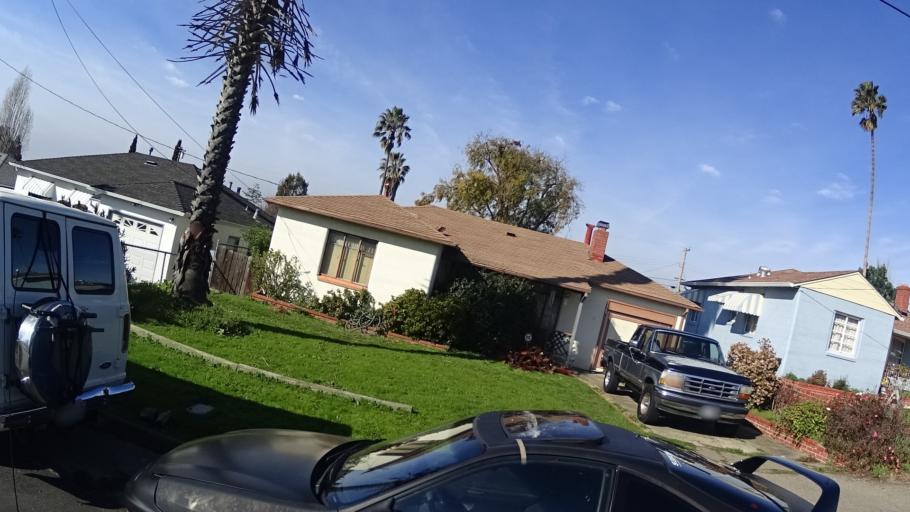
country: US
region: California
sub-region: Alameda County
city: Fairview
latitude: 37.6809
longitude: -122.0539
